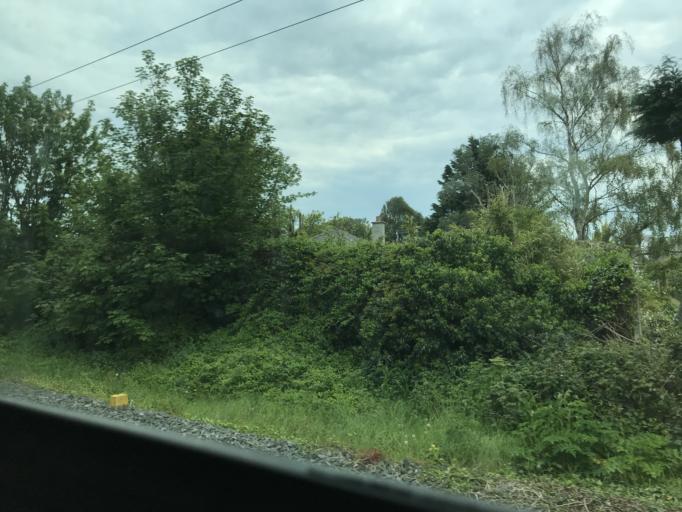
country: IE
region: Leinster
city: Sutton
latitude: 53.3917
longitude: -6.1023
